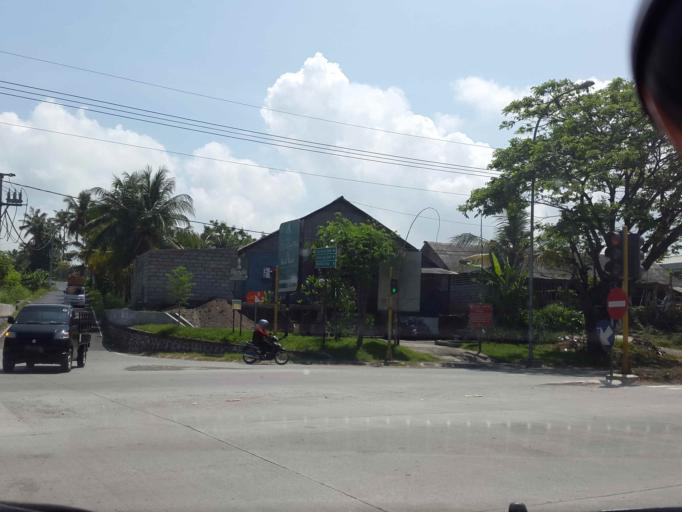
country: ID
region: Bali
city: Klungkung
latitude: -8.5686
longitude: 115.3734
